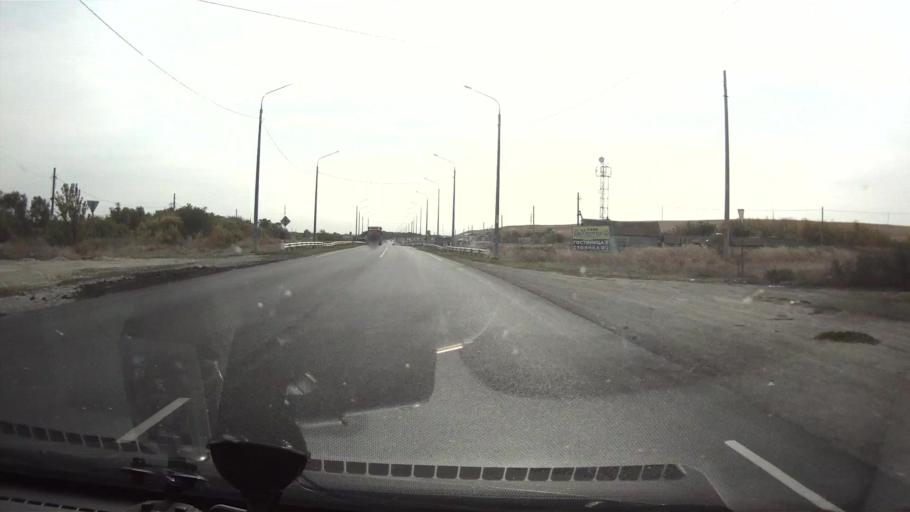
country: RU
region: Saratov
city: Sinodskoye
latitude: 52.0874
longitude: 46.8033
